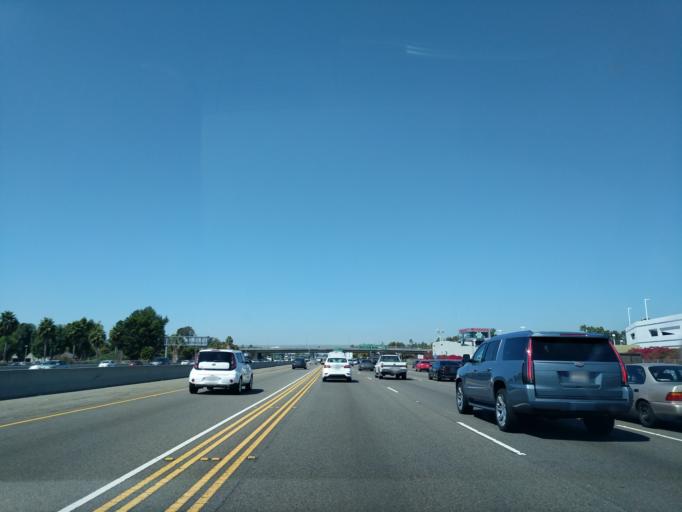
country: US
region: California
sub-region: Orange County
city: Tustin
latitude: 33.7236
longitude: -117.8007
